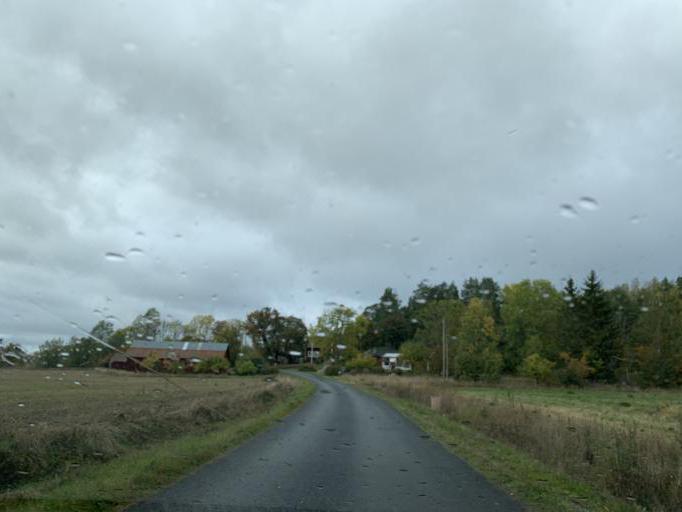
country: SE
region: Soedermanland
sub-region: Eskilstuna Kommun
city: Kvicksund
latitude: 59.3276
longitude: 16.3002
